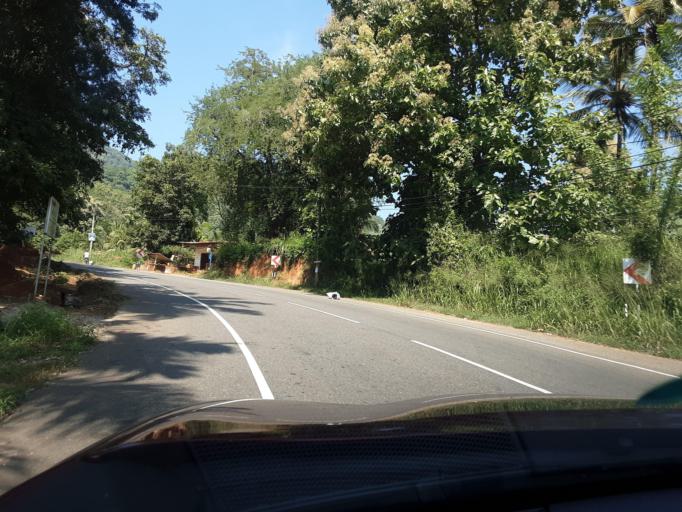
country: LK
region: Uva
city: Badulla
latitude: 7.1582
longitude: 81.0536
